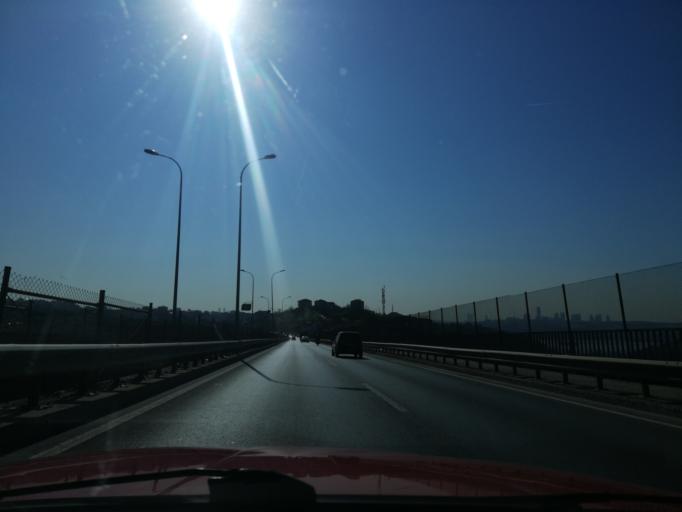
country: TR
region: Istanbul
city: Umraniye
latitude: 41.1057
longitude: 29.1037
